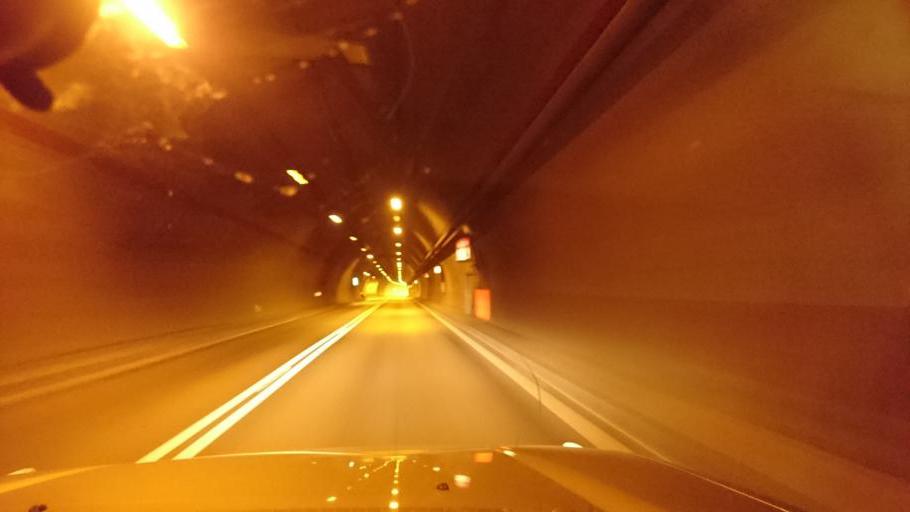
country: IT
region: Lombardy
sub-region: Provincia di Brescia
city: Vobarno
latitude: 45.6416
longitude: 10.4864
